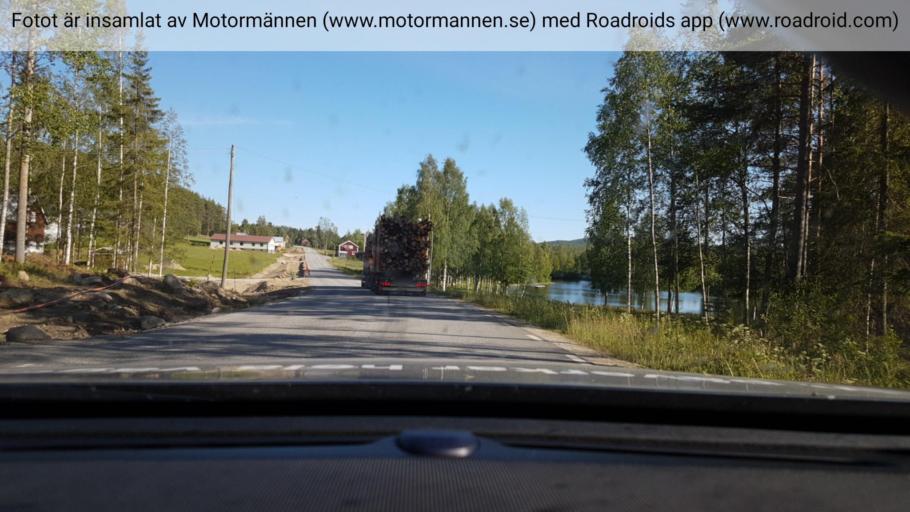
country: SE
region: Vaesterbotten
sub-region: Bjurholms Kommun
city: Bjurholm
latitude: 64.2313
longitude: 19.3522
